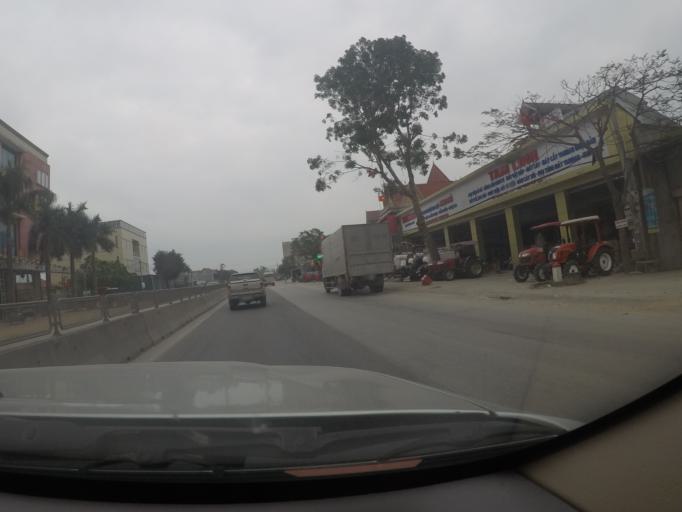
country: VN
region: Nghe An
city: Dien Chau
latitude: 18.9973
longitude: 105.5955
